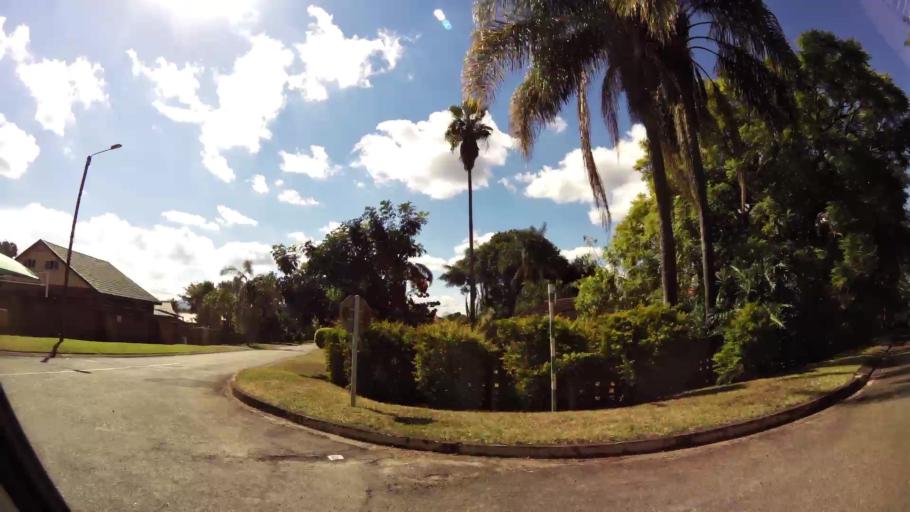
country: ZA
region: Limpopo
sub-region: Mopani District Municipality
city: Tzaneen
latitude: -23.8201
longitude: 30.1455
